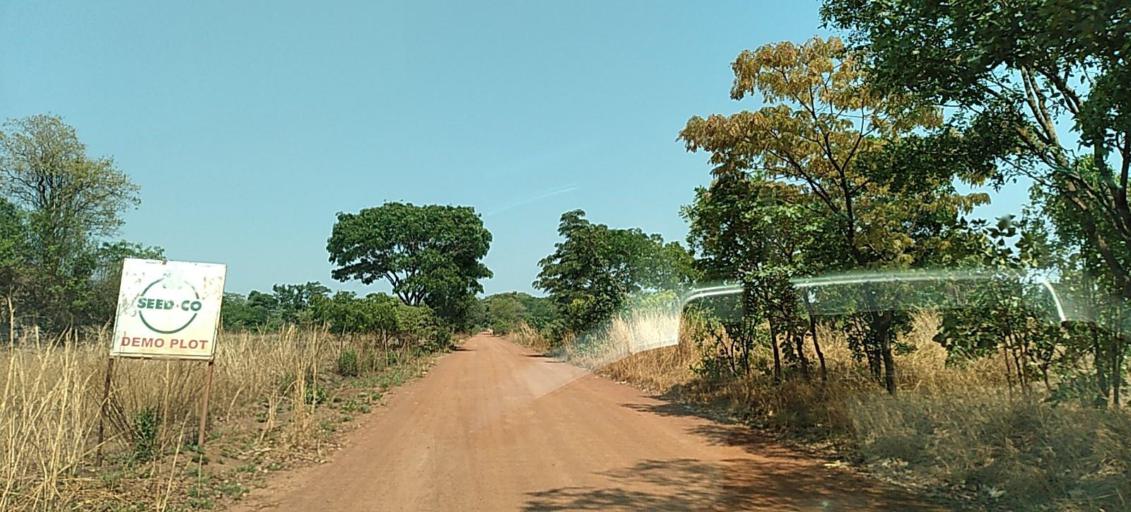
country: ZM
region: Copperbelt
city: Chingola
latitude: -12.5419
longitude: 27.7384
